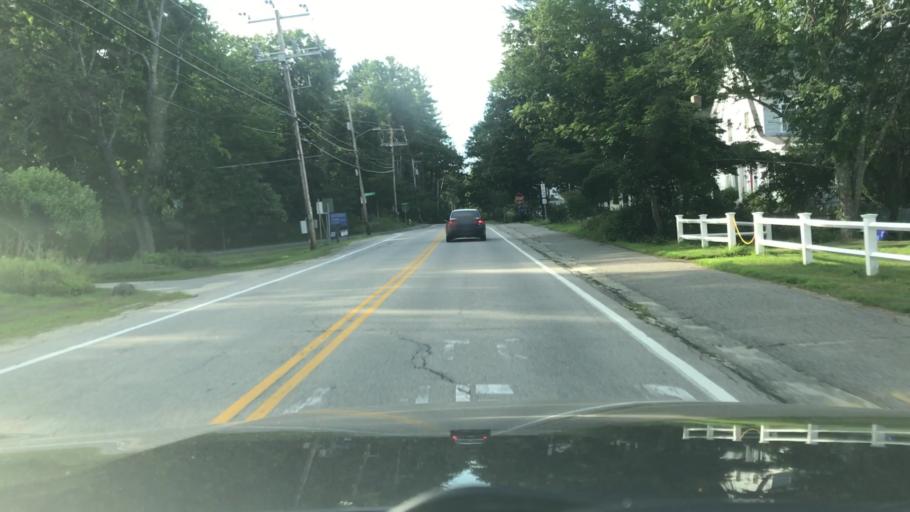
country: US
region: New Hampshire
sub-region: Strafford County
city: Durham
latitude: 43.1433
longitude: -70.9274
